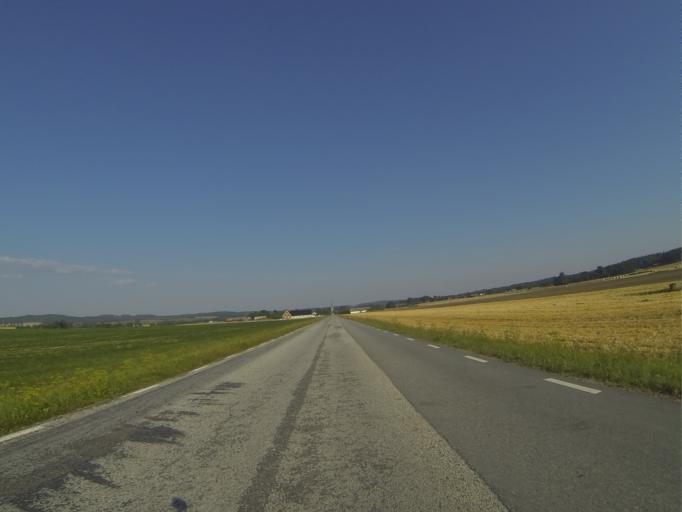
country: SE
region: Skane
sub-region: Lunds Kommun
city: Genarp
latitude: 55.6058
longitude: 13.3733
